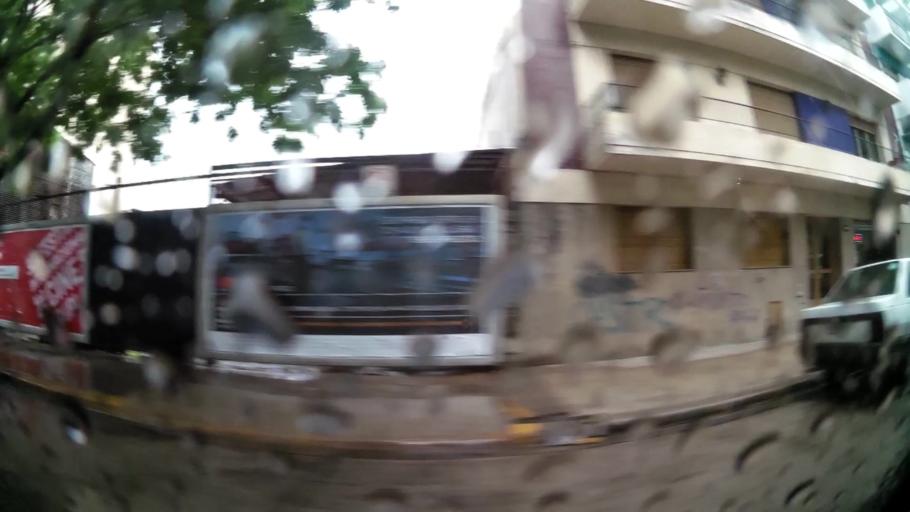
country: AR
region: Buenos Aires
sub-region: Partido de Avellaneda
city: Avellaneda
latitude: -34.6359
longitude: -58.3622
